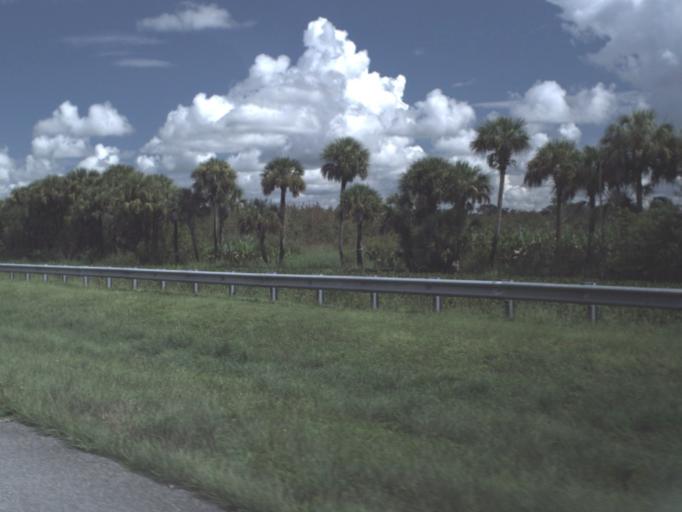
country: US
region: Florida
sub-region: Collier County
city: Immokalee
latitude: 26.2062
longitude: -81.3462
